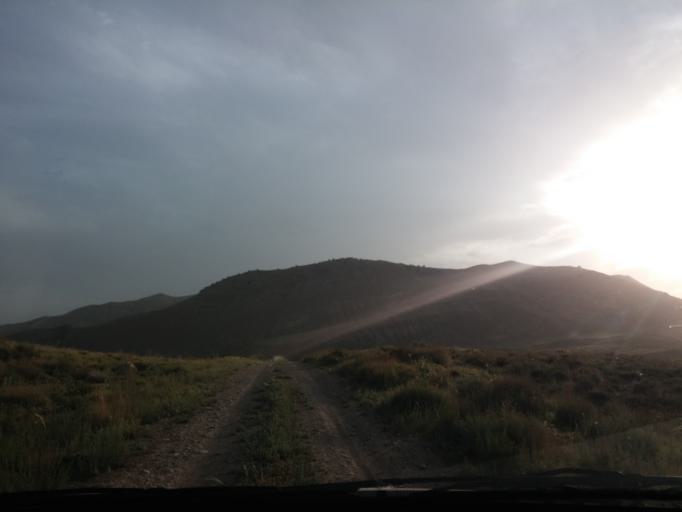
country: IR
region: Semnan
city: Istgah-e Rah Ahan-e Garmsar
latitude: 35.4888
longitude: 52.3001
